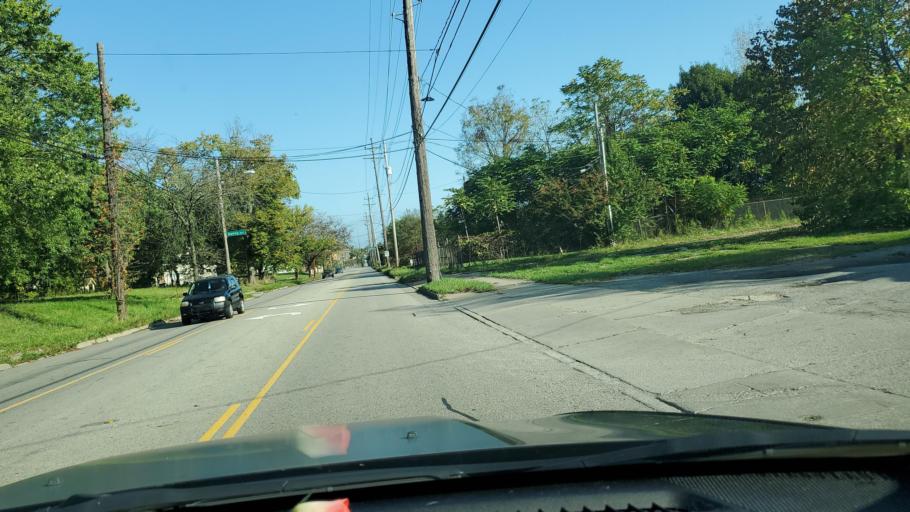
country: US
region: Ohio
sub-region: Mahoning County
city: Youngstown
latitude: 41.1186
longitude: -80.6383
